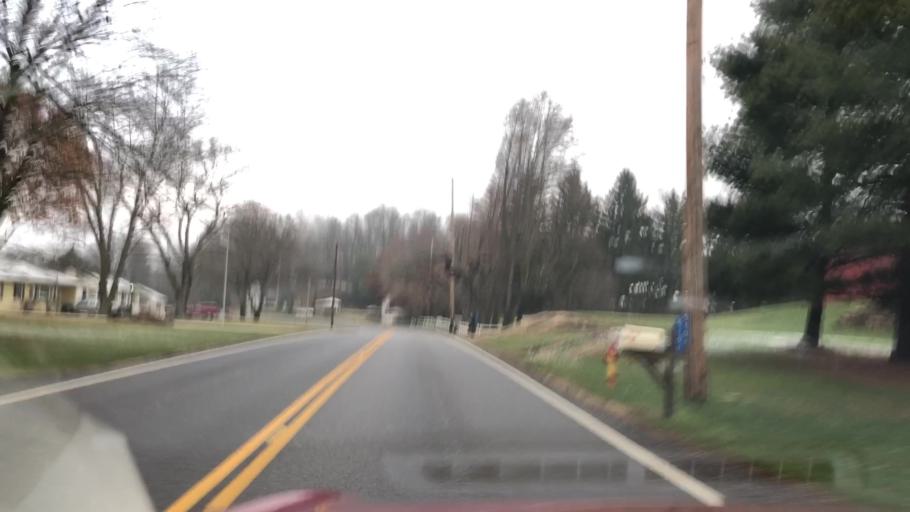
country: US
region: Ohio
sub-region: Stark County
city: Massillon
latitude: 40.8552
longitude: -81.5206
